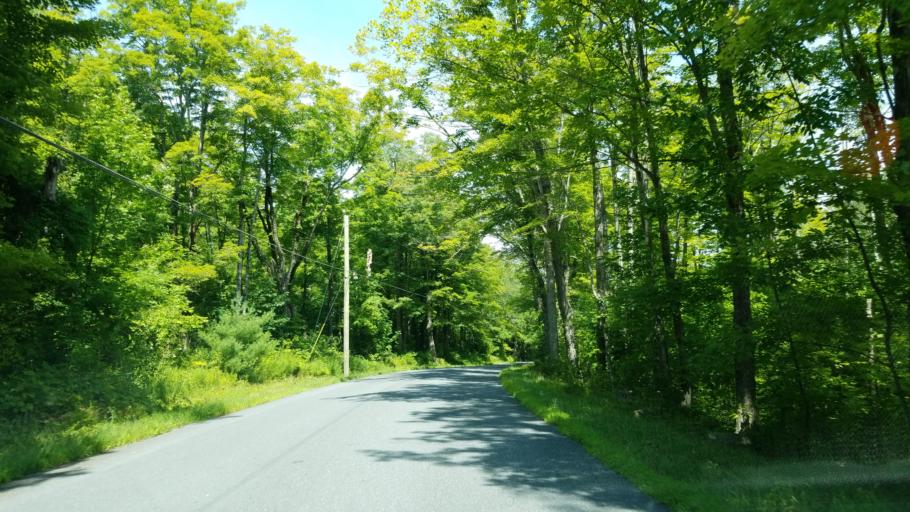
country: US
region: Connecticut
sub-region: Litchfield County
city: Winchester Center
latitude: 41.8842
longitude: -73.2090
